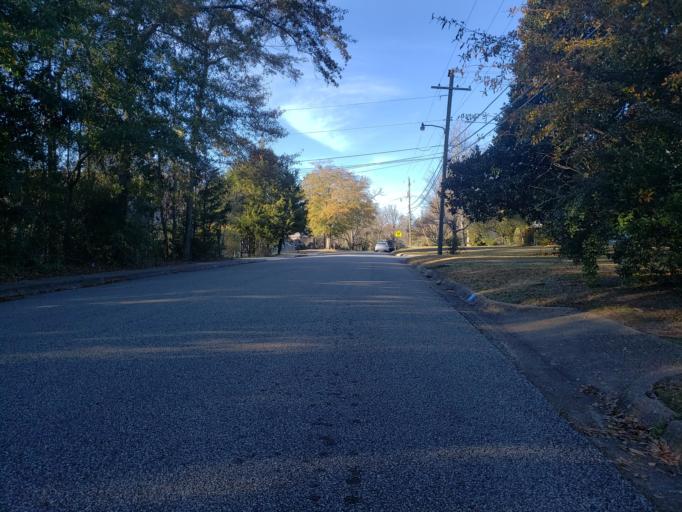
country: US
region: Alabama
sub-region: Lee County
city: Auburn
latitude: 32.5958
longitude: -85.4744
